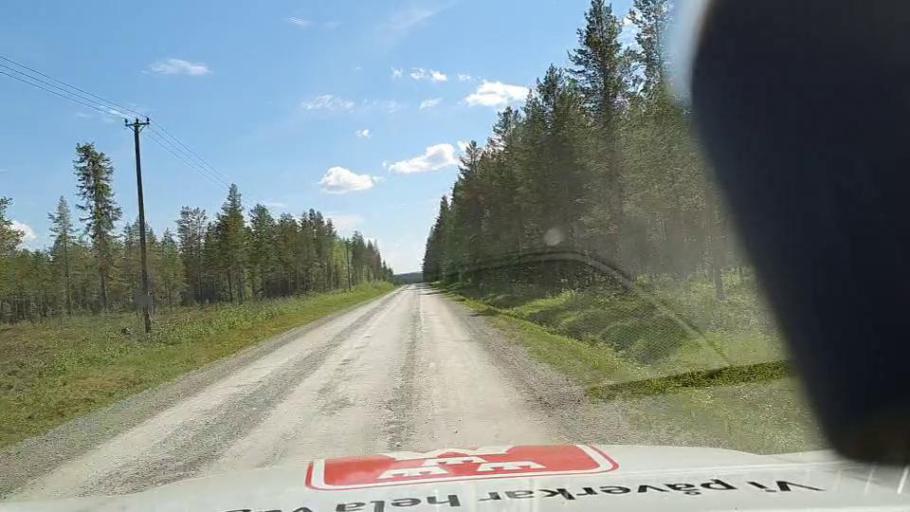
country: SE
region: Jaemtland
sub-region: Stroemsunds Kommun
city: Stroemsund
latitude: 64.4762
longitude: 15.5932
